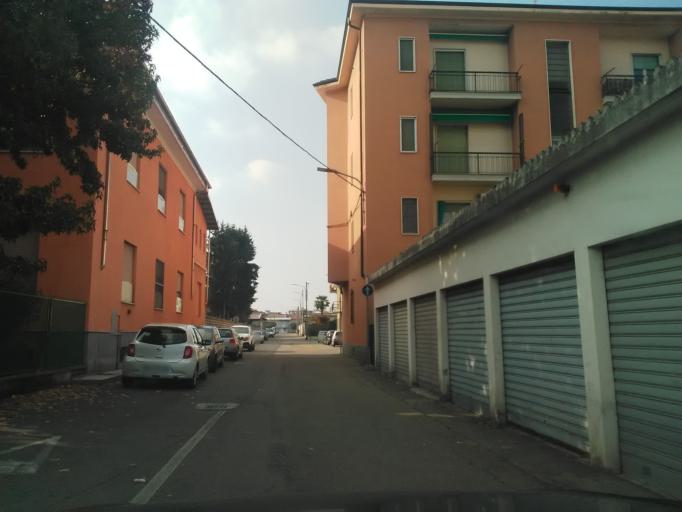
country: IT
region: Piedmont
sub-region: Provincia di Vercelli
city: Santhia
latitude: 45.3671
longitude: 8.1673
